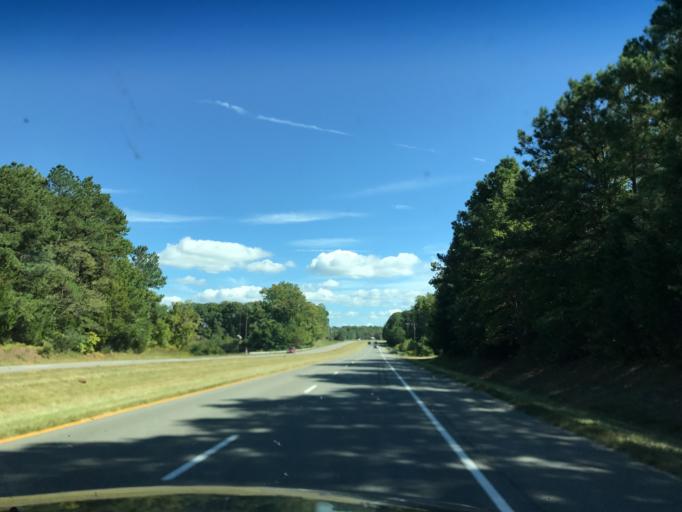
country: US
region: Virginia
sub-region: Essex County
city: Tappahannock
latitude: 37.8550
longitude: -76.8154
